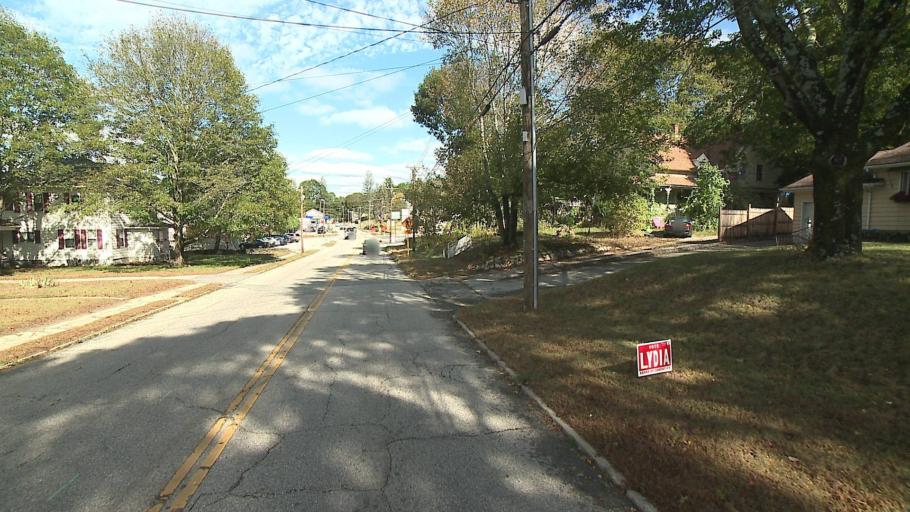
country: US
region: Connecticut
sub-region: Windham County
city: Danielson
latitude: 41.8149
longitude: -71.8767
